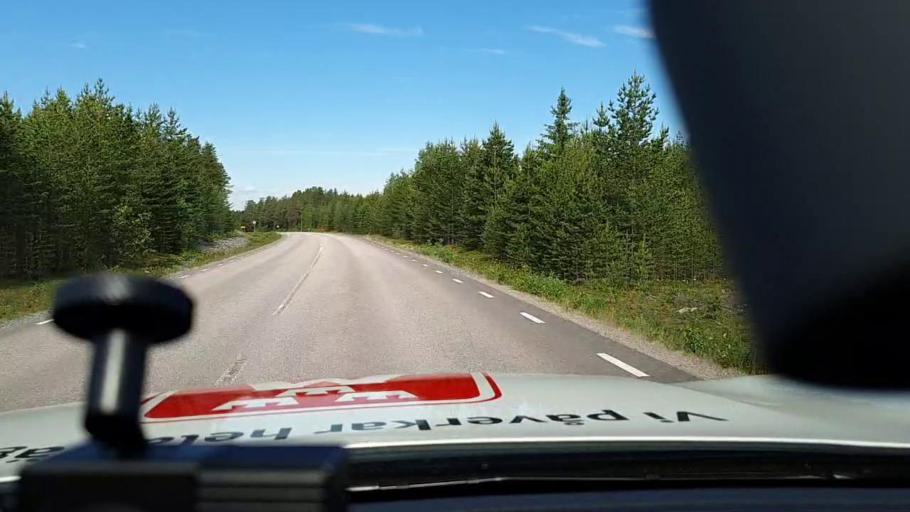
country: SE
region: Norrbotten
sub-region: Lulea Kommun
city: Sodra Sunderbyn
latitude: 65.6339
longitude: 21.9212
